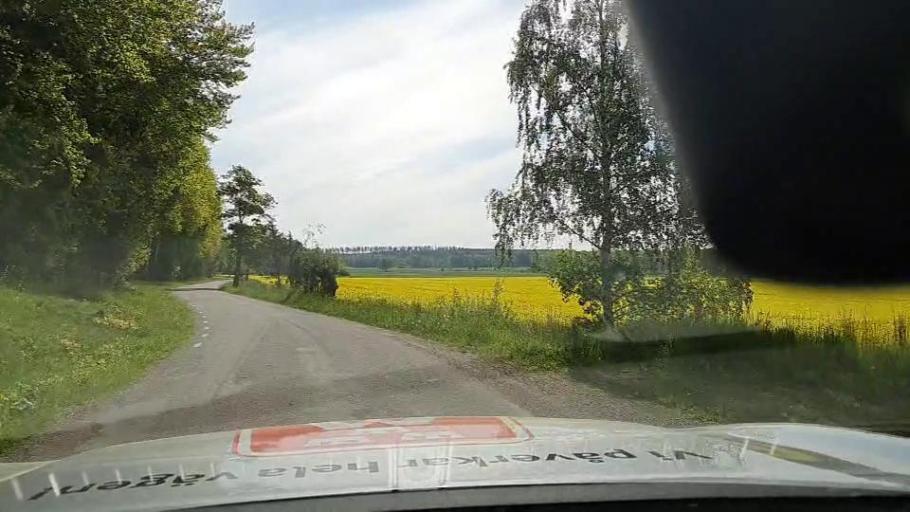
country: SE
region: Soedermanland
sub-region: Eskilstuna Kommun
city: Arla
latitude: 59.2568
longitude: 16.6830
